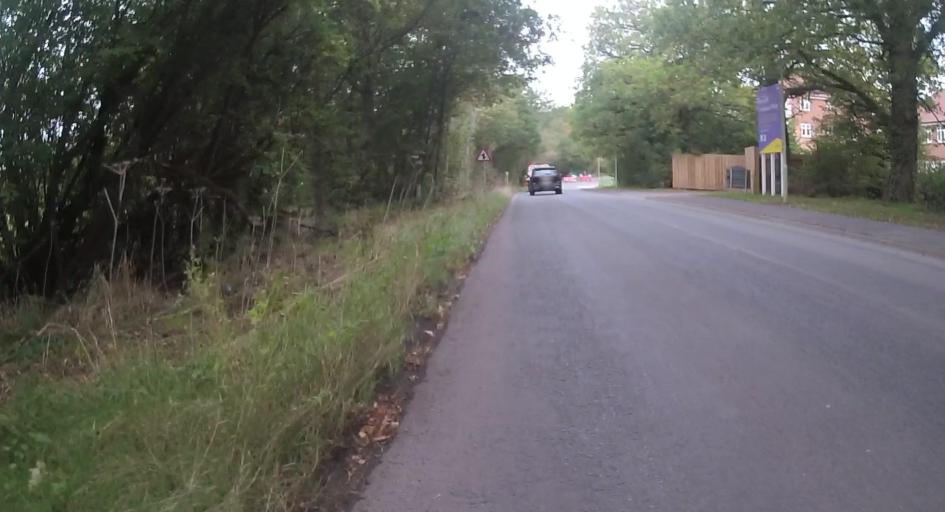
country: GB
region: England
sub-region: Hampshire
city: Fleet
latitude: 51.2731
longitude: -0.8637
